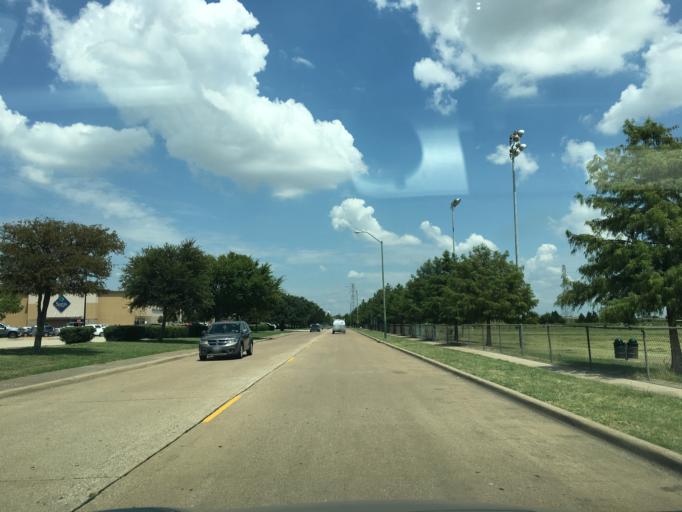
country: US
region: Texas
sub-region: Dallas County
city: Garland
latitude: 32.8660
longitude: -96.6743
